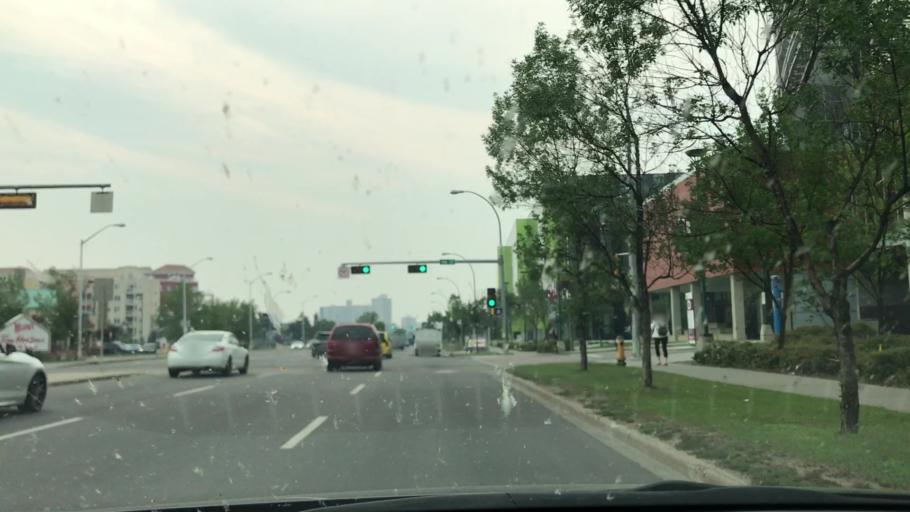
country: CA
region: Alberta
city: Edmonton
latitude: 53.5463
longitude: -113.5096
